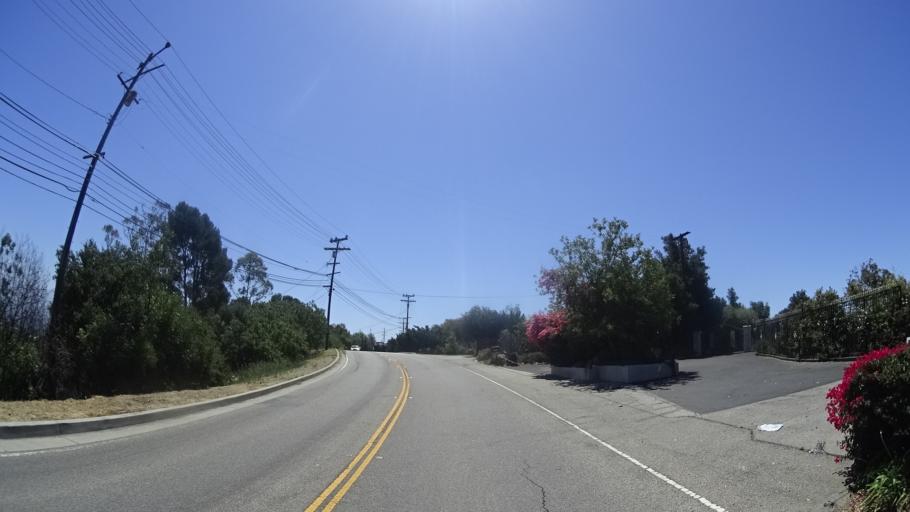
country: US
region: California
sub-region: Los Angeles County
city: Sherman Oaks
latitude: 34.1322
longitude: -118.4537
